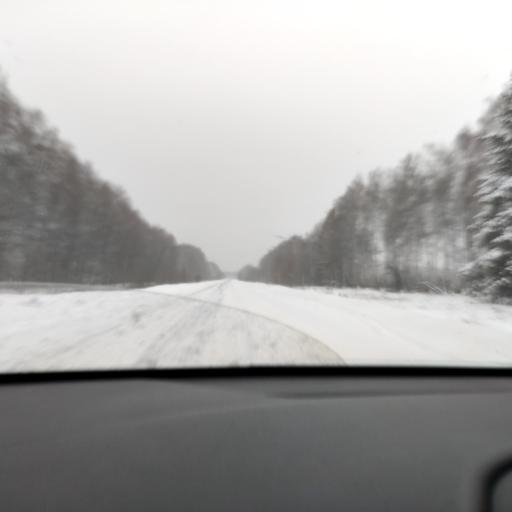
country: RU
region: Tatarstan
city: Vysokaya Gora
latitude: 55.9657
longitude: 49.1714
